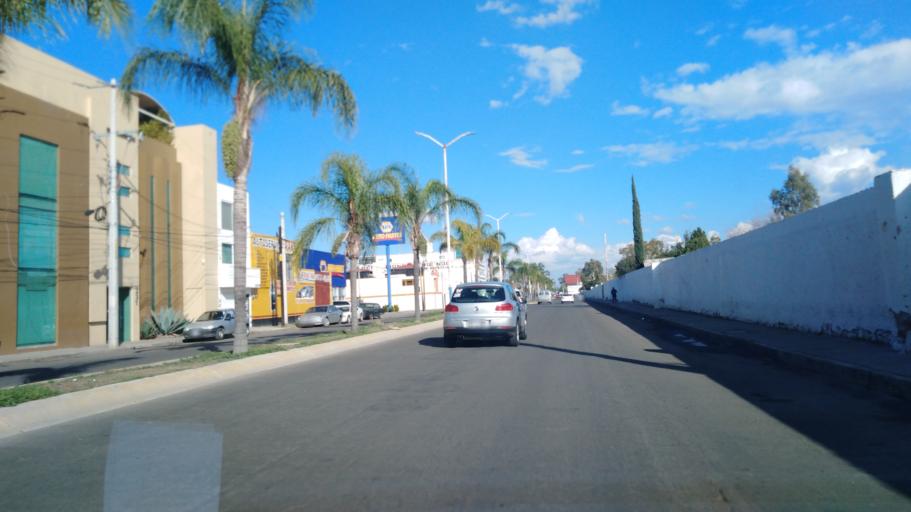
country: MX
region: Durango
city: Victoria de Durango
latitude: 24.0302
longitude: -104.6383
